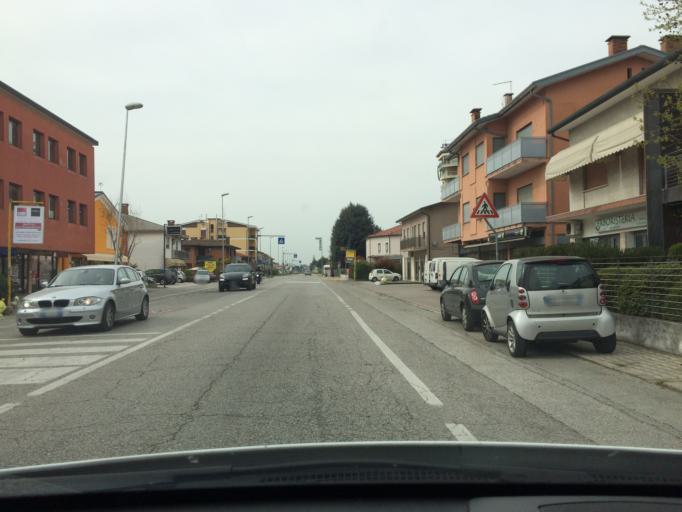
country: IT
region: Veneto
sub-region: Provincia di Padova
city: Cittadella
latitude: 45.6465
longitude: 11.7716
